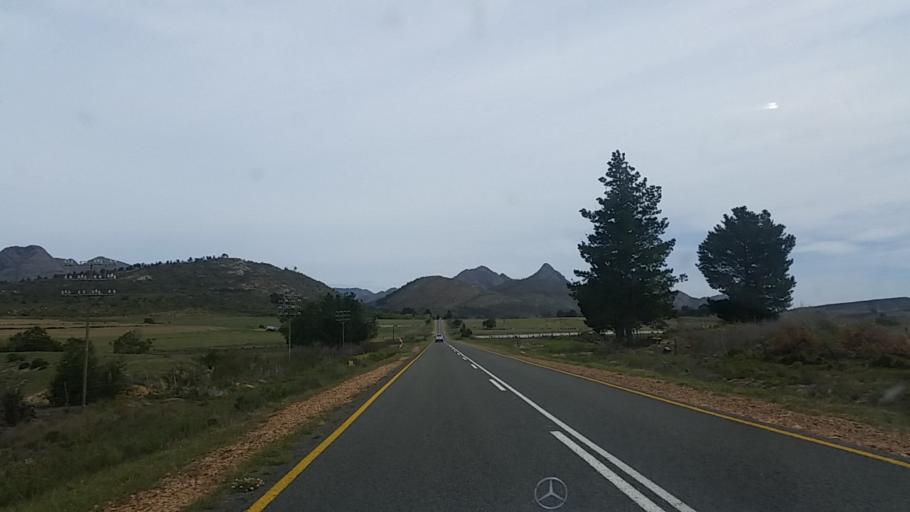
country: ZA
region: Western Cape
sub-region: Eden District Municipality
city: George
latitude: -33.8293
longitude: 22.4654
